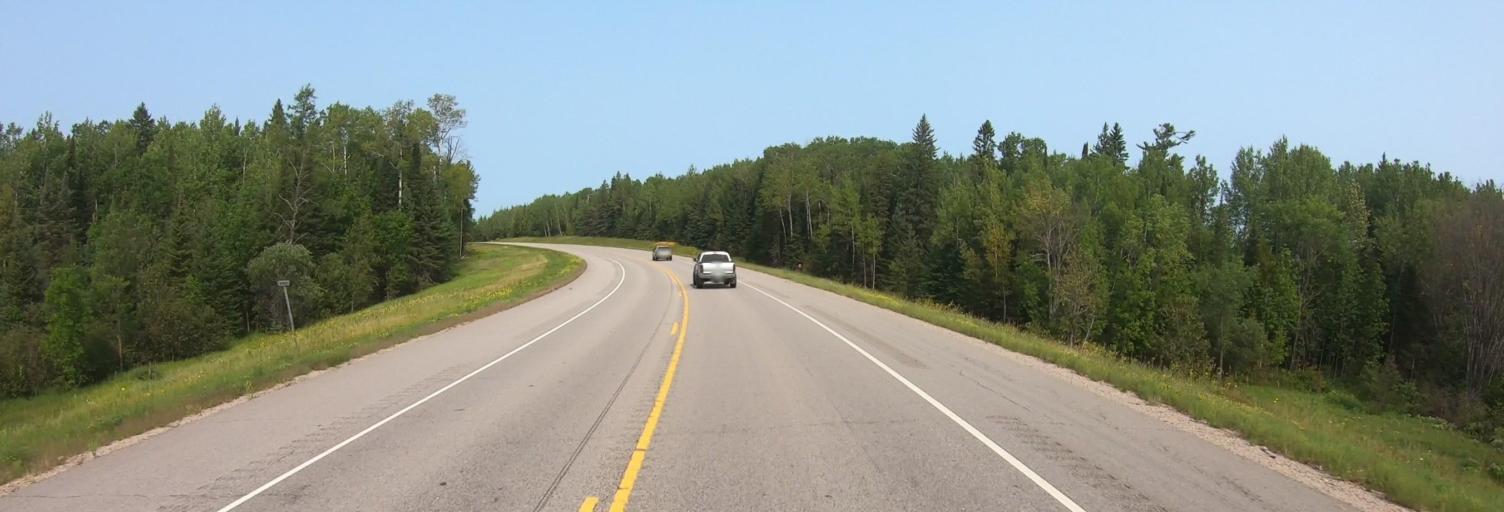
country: CA
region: Ontario
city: Fort Frances
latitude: 48.3643
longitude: -92.9634
